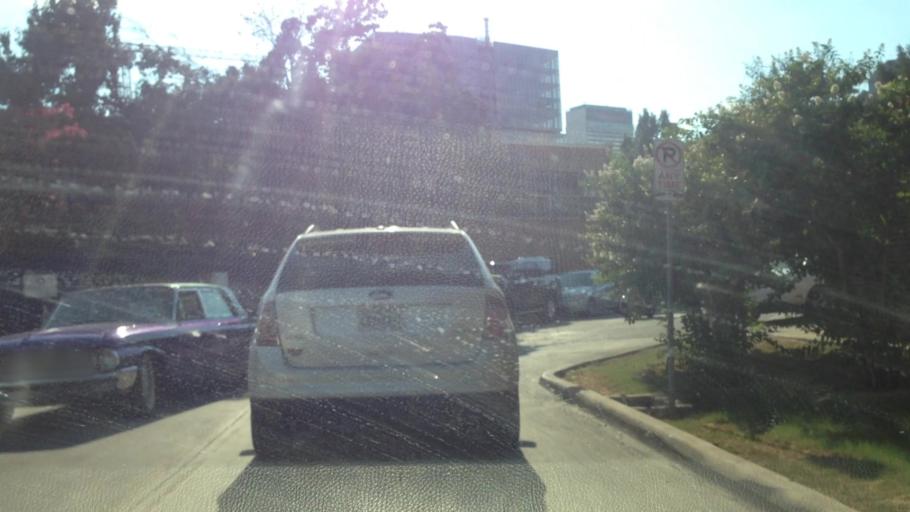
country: US
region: Texas
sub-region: Dallas County
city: Dallas
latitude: 32.7852
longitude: -96.7846
